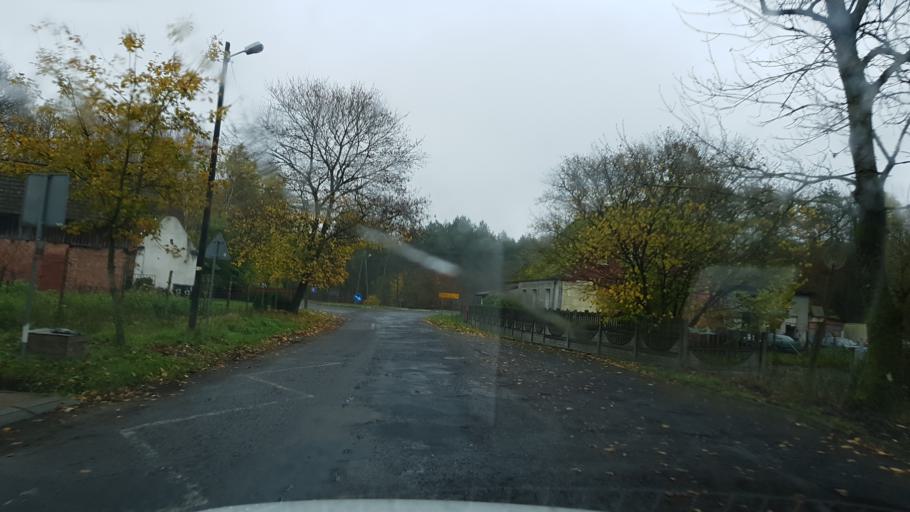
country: PL
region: West Pomeranian Voivodeship
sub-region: Powiat goleniowski
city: Przybiernow
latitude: 53.6643
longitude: 14.7463
